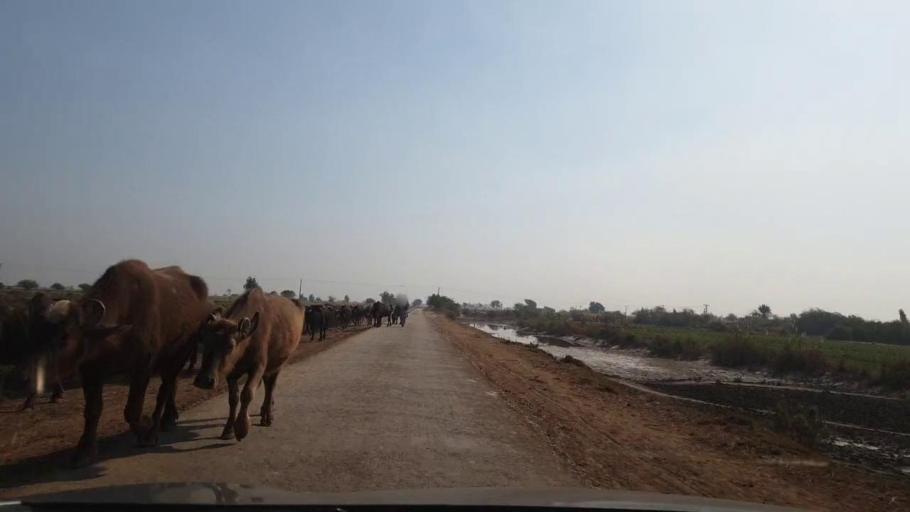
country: PK
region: Sindh
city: Berani
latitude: 25.6464
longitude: 68.8907
